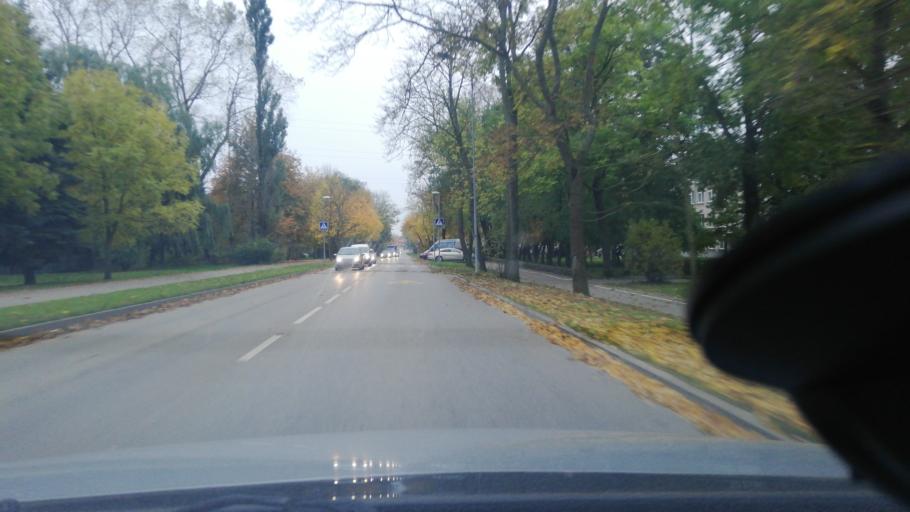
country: LT
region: Klaipedos apskritis
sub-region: Klaipeda
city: Klaipeda
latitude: 55.7276
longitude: 21.1318
